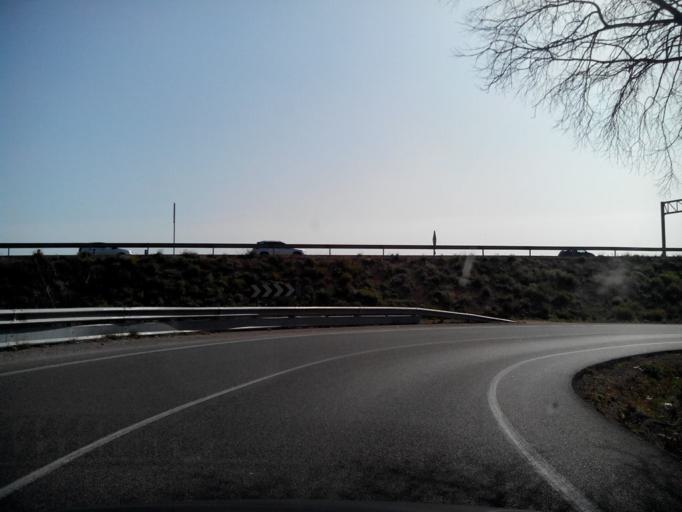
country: ES
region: Catalonia
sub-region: Provincia de Tarragona
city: Alcover
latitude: 41.2613
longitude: 1.1755
